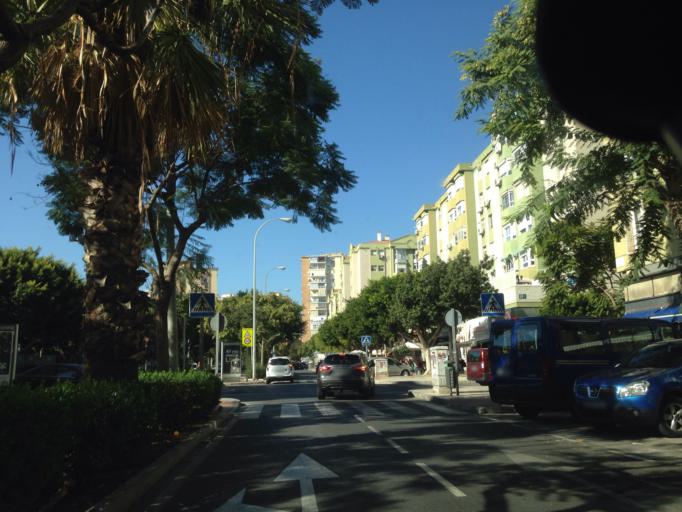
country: ES
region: Andalusia
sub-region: Provincia de Malaga
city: Malaga
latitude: 36.7039
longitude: -4.4347
